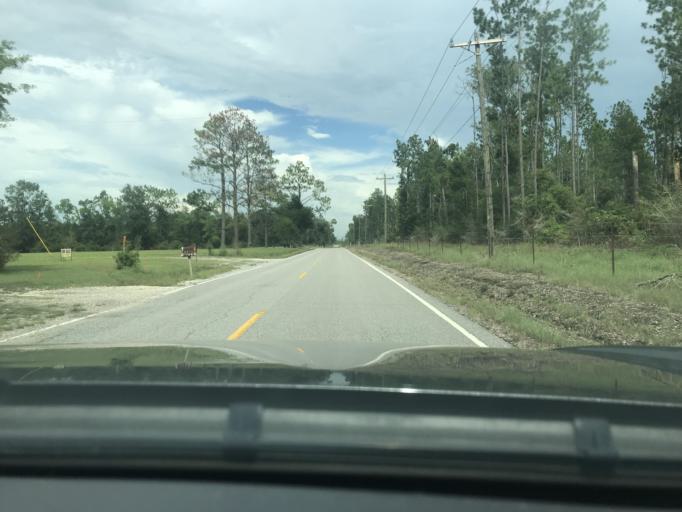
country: US
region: Louisiana
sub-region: Calcasieu Parish
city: Moss Bluff
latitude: 30.3886
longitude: -93.2446
